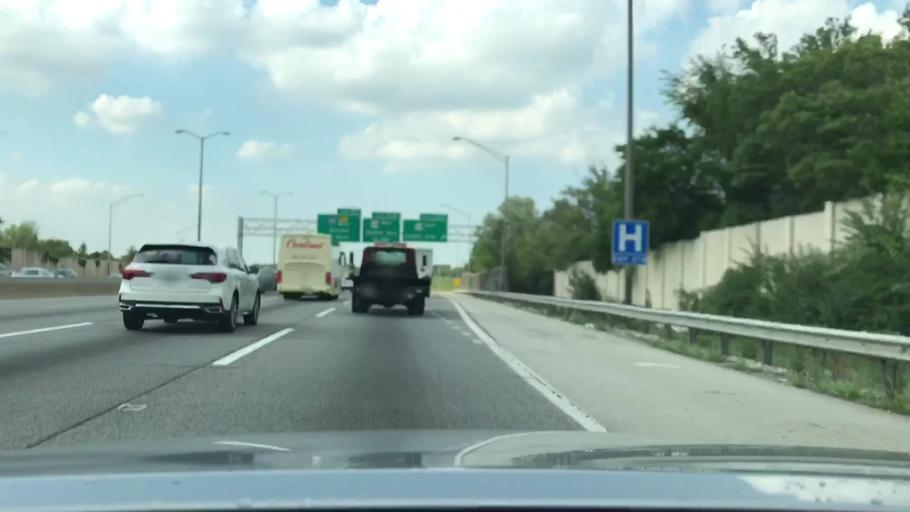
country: US
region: Illinois
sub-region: Cook County
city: Western Springs
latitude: 41.8140
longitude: -87.9137
